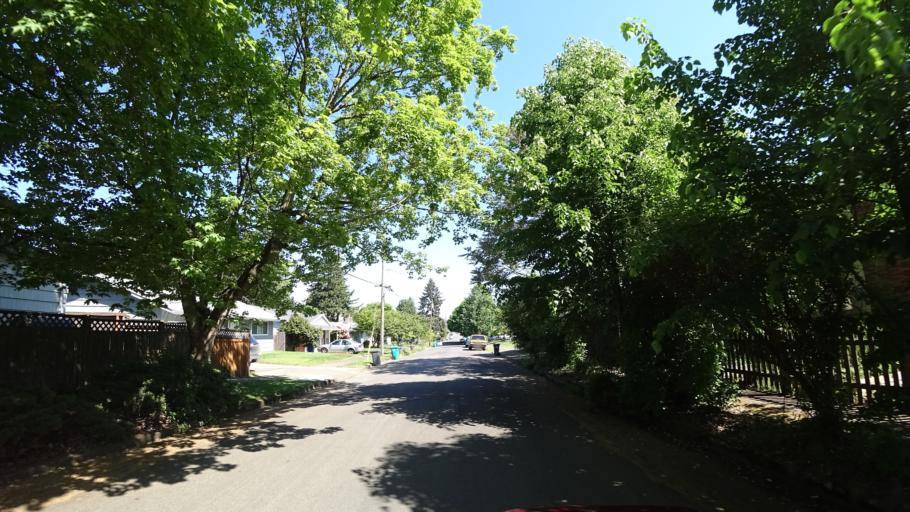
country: US
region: Oregon
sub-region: Multnomah County
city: Lents
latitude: 45.4936
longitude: -122.6114
